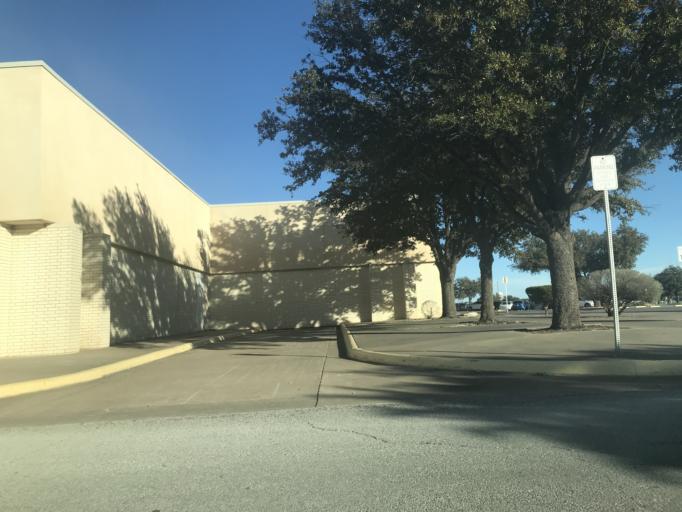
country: US
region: Texas
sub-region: Tom Green County
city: San Angelo
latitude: 31.4279
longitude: -100.5017
